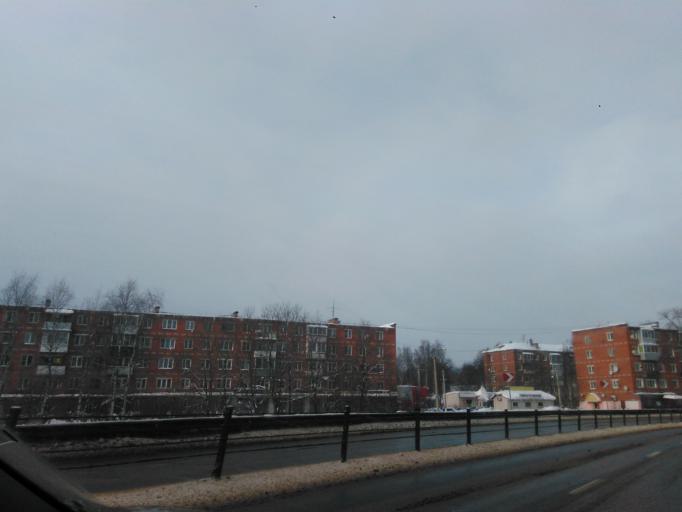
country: RU
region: Moskovskaya
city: Dedenevo
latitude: 56.2371
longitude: 37.5237
